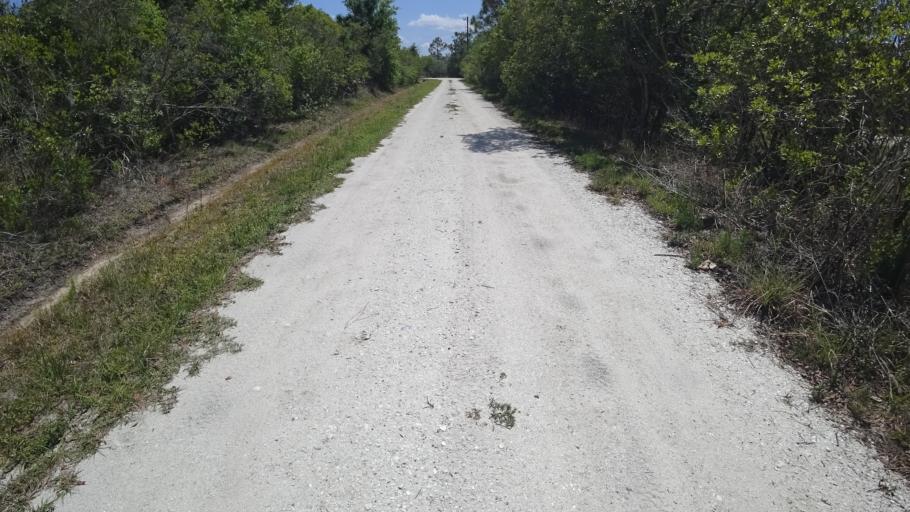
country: US
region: Florida
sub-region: Sarasota County
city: The Meadows
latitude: 27.4264
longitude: -82.3161
